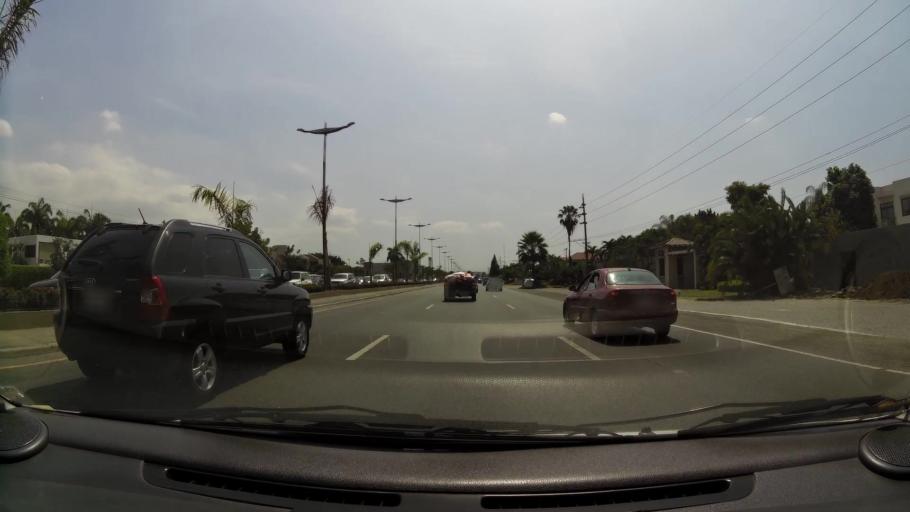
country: EC
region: Guayas
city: Eloy Alfaro
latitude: -2.1165
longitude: -79.8684
